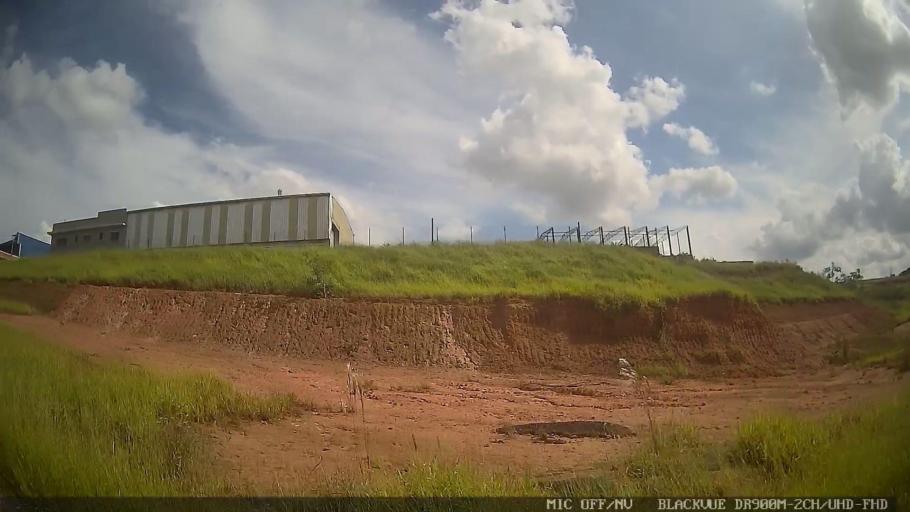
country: BR
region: Sao Paulo
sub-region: Atibaia
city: Atibaia
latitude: -23.0726
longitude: -46.5714
